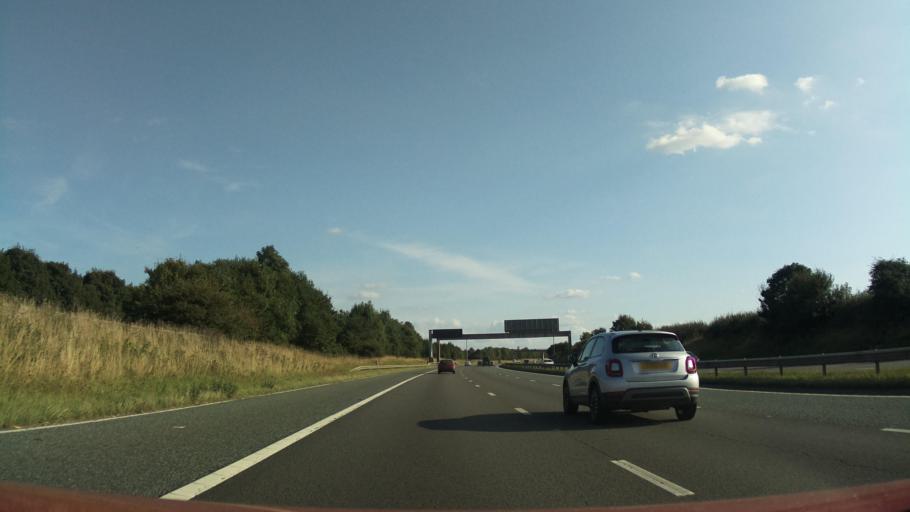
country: GB
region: England
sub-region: North Yorkshire
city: Boroughbridge
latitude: 54.1298
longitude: -1.4166
